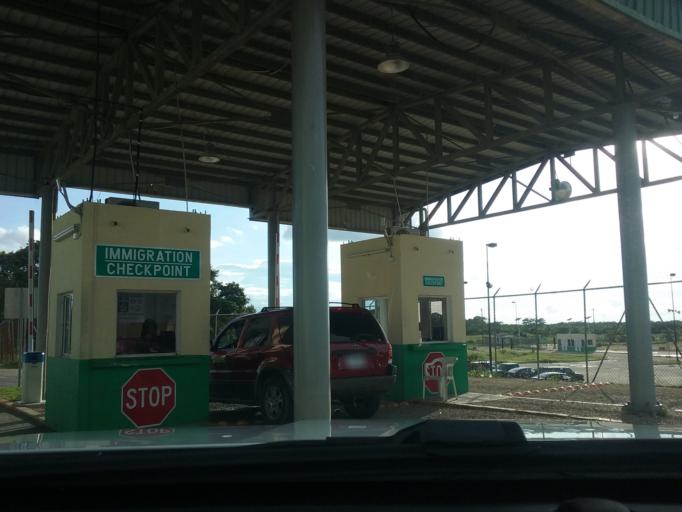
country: BZ
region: Corozal
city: Corozal
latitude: 18.4857
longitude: -88.3997
